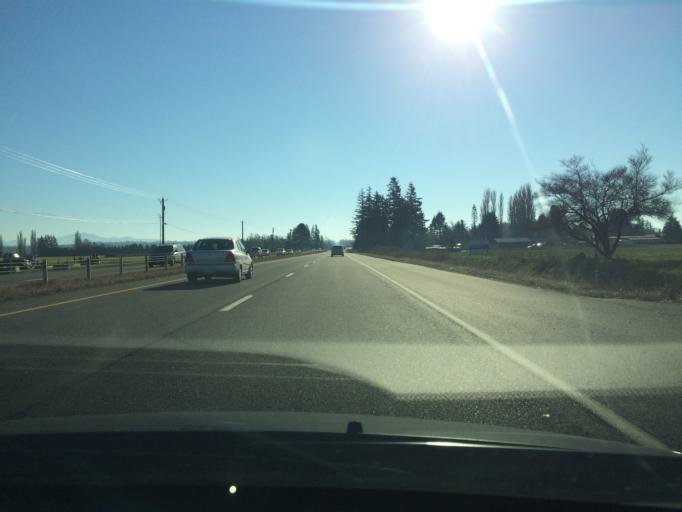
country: US
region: Washington
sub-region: Whatcom County
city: Lynden
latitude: 48.8845
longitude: -122.4857
